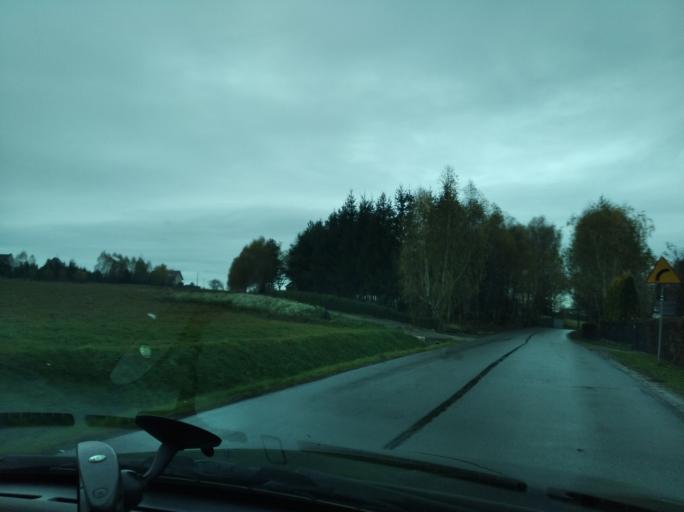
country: PL
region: Subcarpathian Voivodeship
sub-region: Powiat rzeszowski
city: Tyczyn
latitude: 49.9234
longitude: 22.0287
